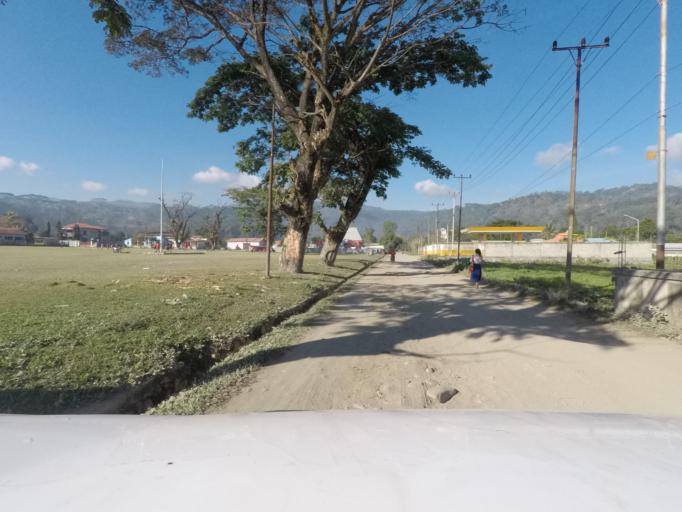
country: TL
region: Ermera
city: Gleno
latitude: -8.7231
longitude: 125.4316
